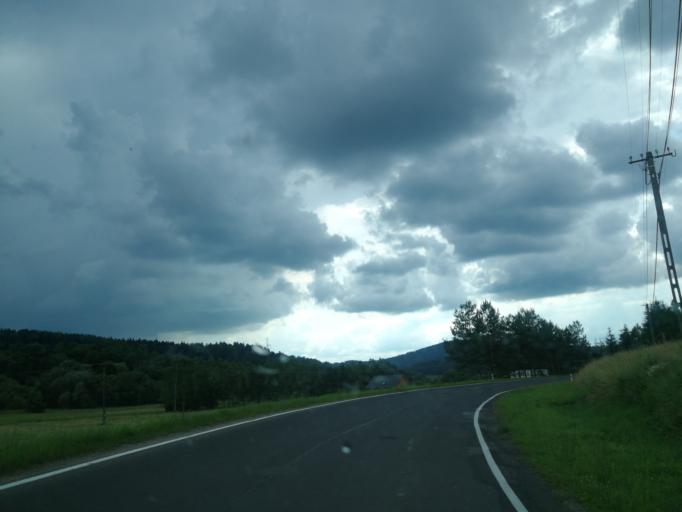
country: PL
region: Subcarpathian Voivodeship
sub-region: Powiat leski
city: Uherce Mineralne
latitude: 49.4526
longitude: 22.4255
